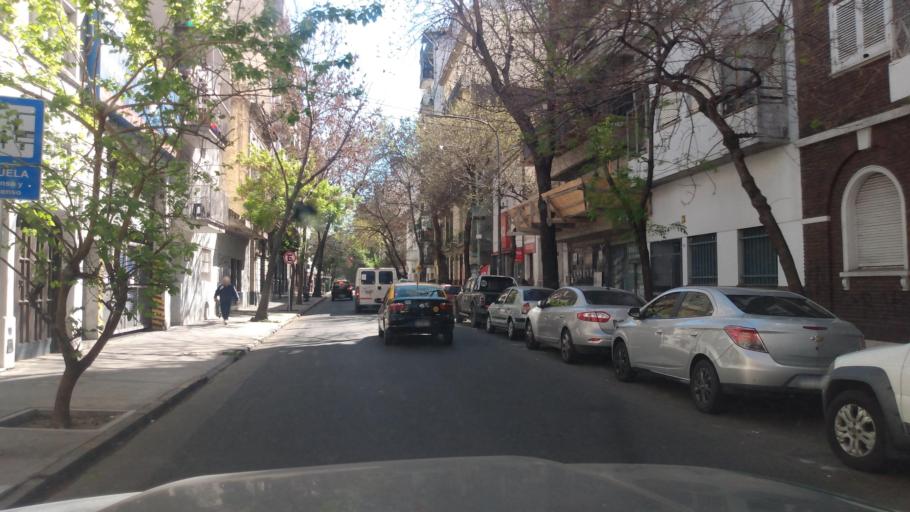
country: AR
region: Buenos Aires F.D.
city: Buenos Aires
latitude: -34.6129
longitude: -58.3948
